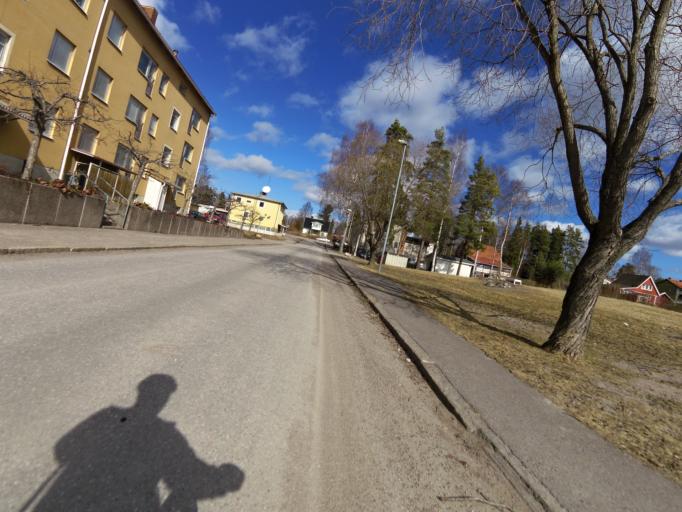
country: SE
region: Gaevleborg
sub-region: Hofors Kommun
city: Hofors
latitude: 60.5404
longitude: 16.2833
